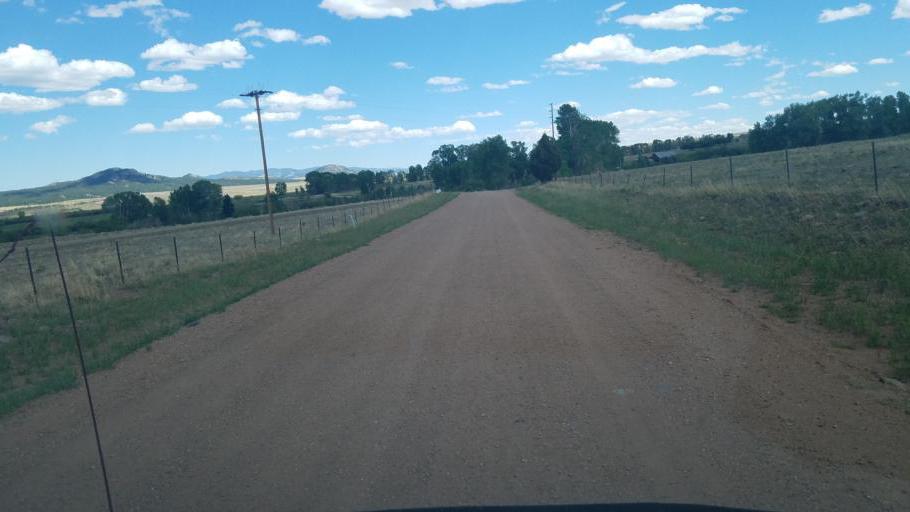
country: US
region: Colorado
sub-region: Custer County
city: Westcliffe
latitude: 38.2420
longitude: -105.6047
